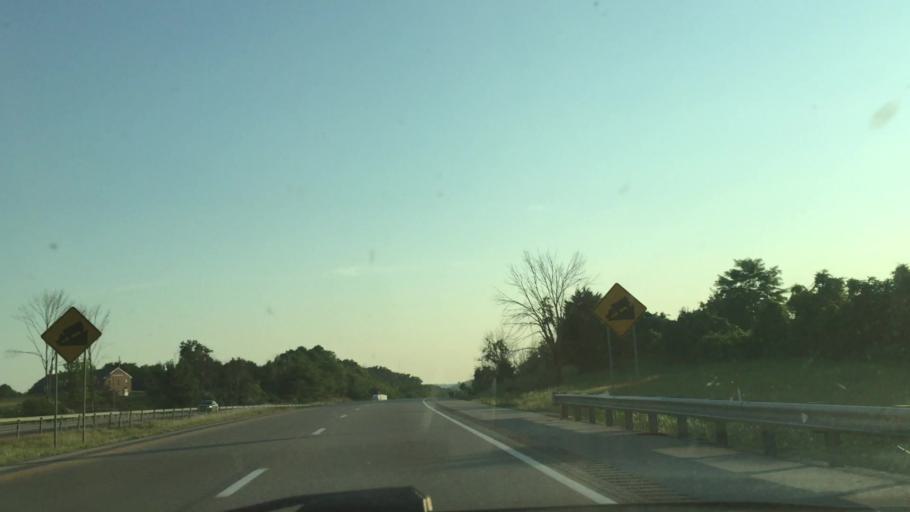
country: US
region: Kentucky
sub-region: Gallatin County
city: Warsaw
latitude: 38.7632
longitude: -84.7899
